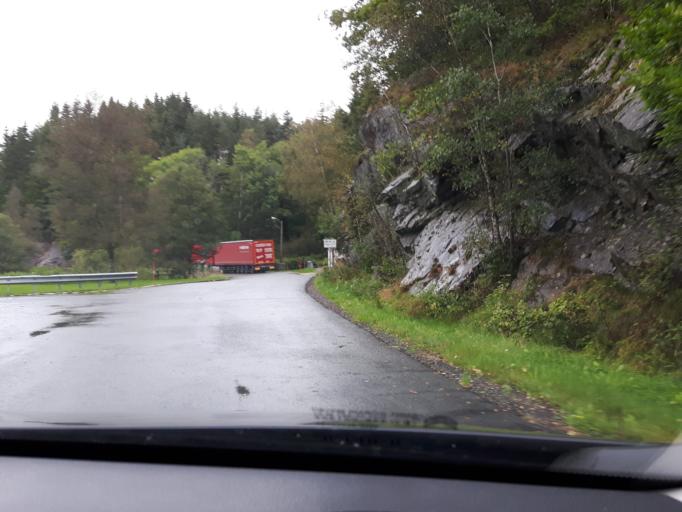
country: NO
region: Vest-Agder
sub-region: Marnardal
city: Helland
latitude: 58.0861
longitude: 7.6201
